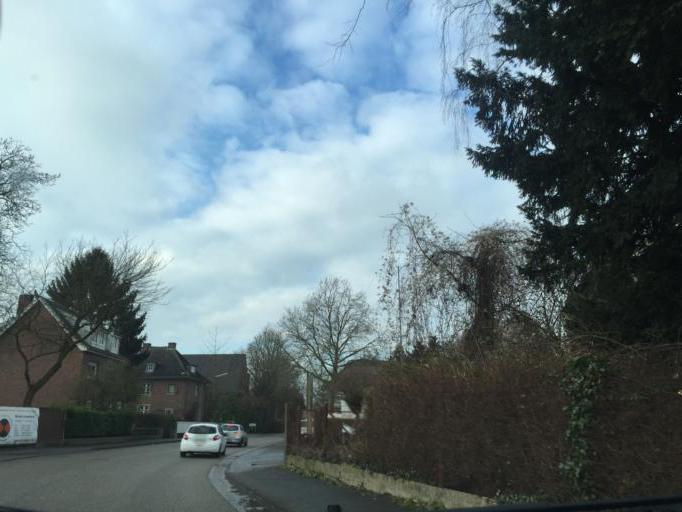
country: DE
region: North Rhine-Westphalia
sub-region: Regierungsbezirk Dusseldorf
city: Kleve
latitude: 51.7926
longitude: 6.1393
